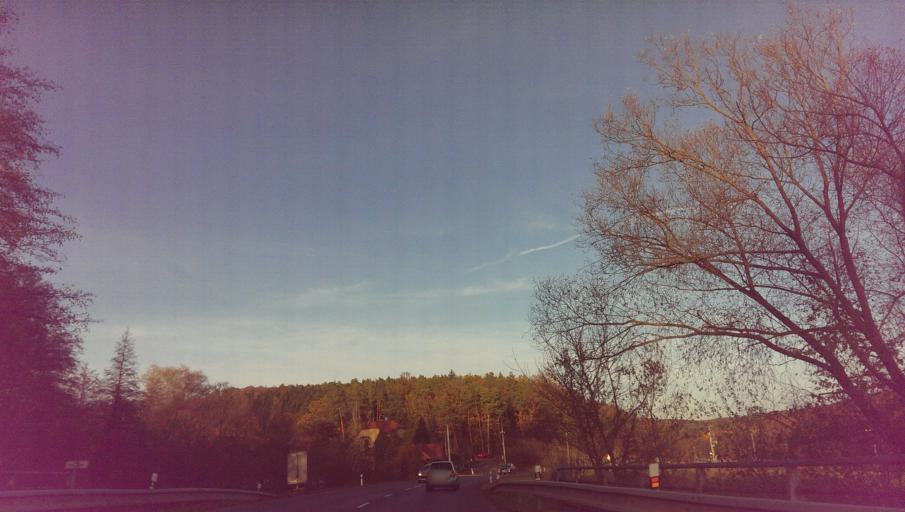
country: CZ
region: Zlin
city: Brezolupy
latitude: 49.1303
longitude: 17.5902
